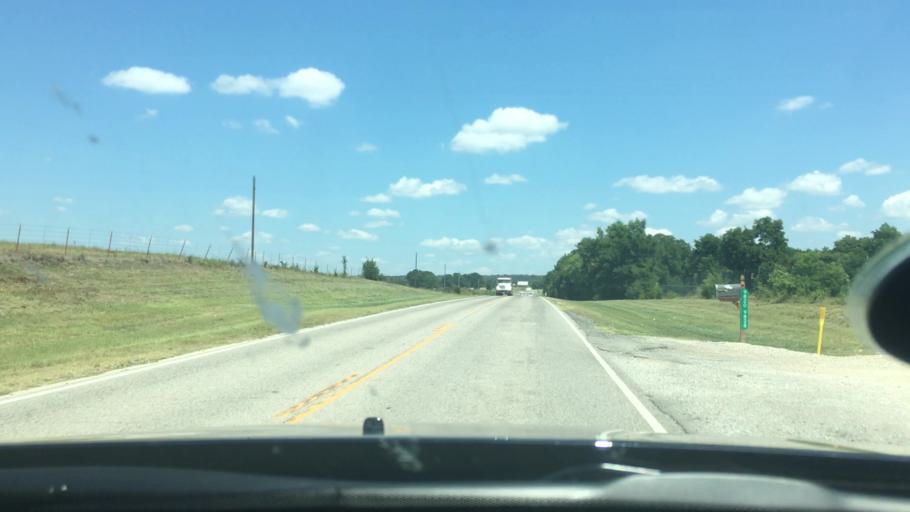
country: US
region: Oklahoma
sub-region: Carter County
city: Dickson
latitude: 34.2828
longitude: -96.9682
